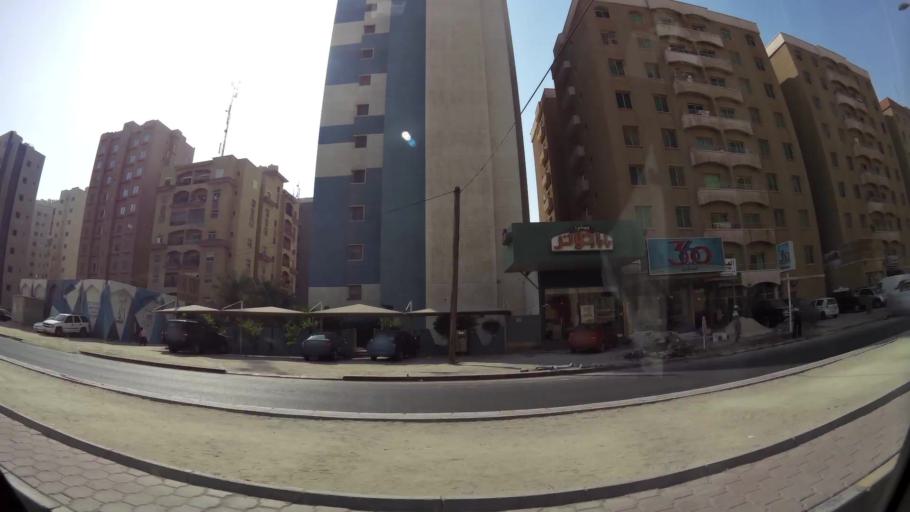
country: KW
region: Al Ahmadi
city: Al Mahbulah
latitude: 29.1468
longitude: 48.1208
